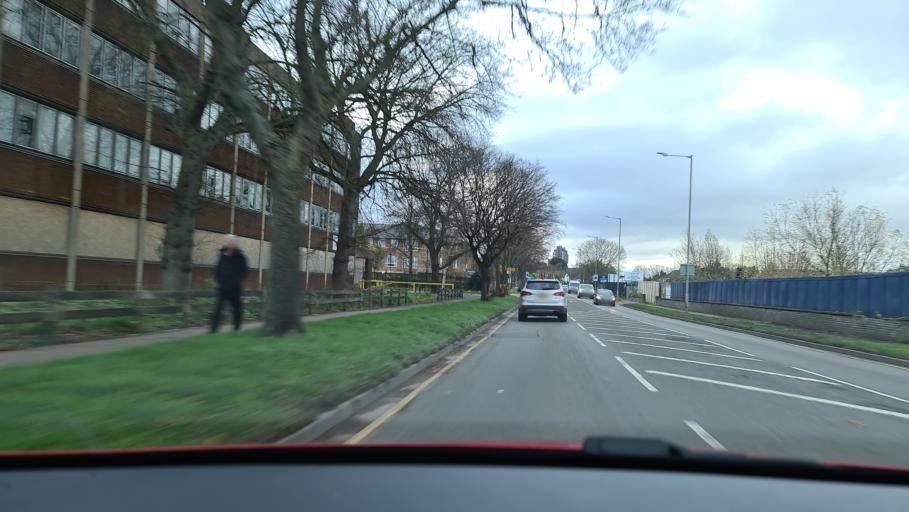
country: GB
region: England
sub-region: Buckinghamshire
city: Aylesbury
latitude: 51.8196
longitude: -0.8238
